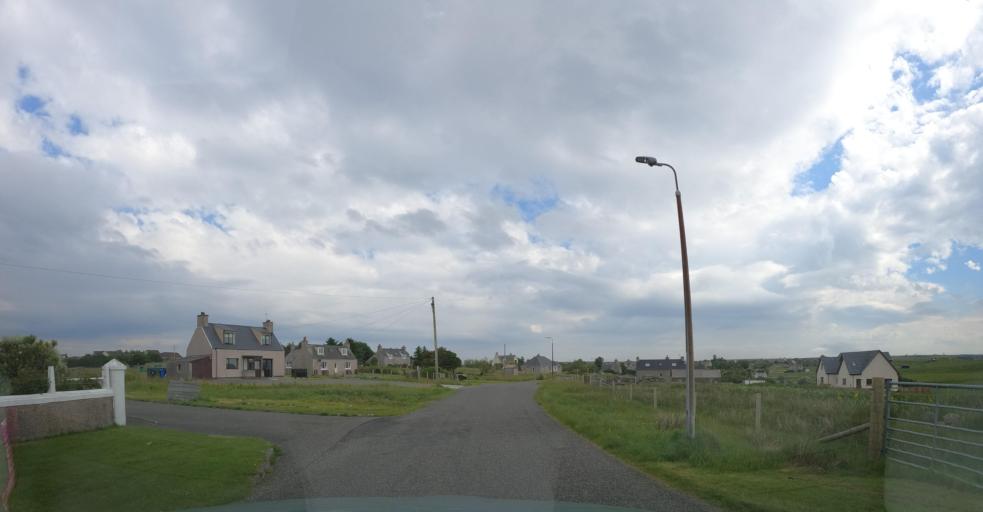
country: GB
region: Scotland
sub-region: Eilean Siar
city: Stornoway
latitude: 58.1995
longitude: -6.2247
